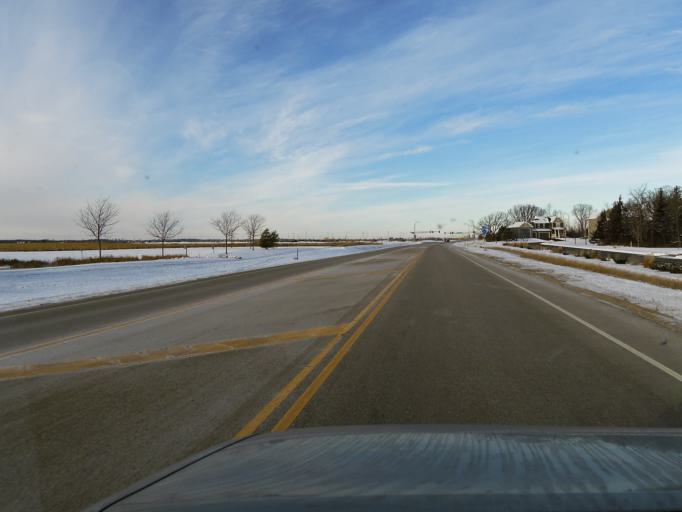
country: US
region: Minnesota
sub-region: Scott County
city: Prior Lake
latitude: 44.7668
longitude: -93.4321
